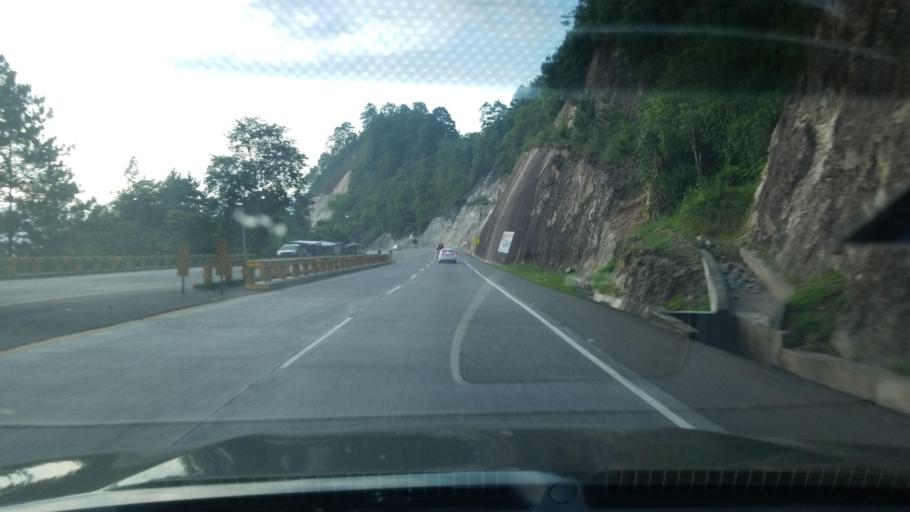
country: HN
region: Comayagua
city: Taulabe
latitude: 14.6623
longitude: -87.9490
